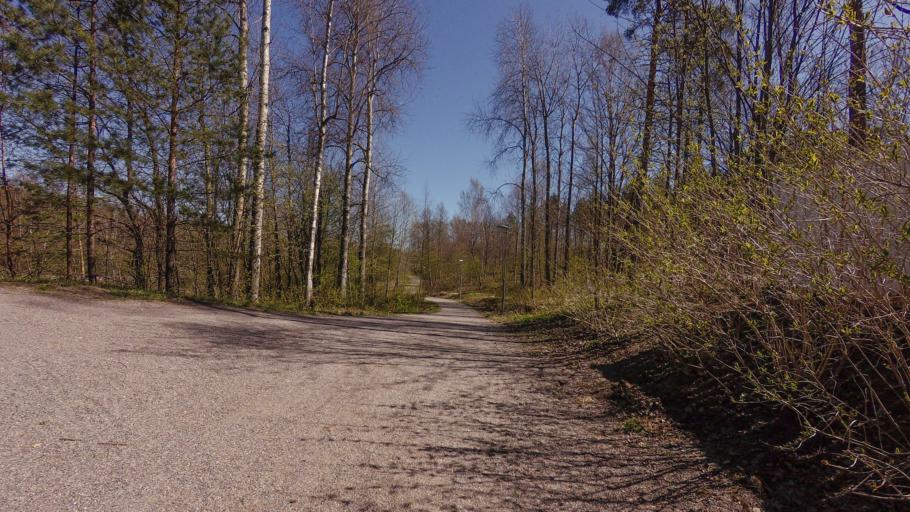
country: FI
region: Uusimaa
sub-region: Helsinki
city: Vantaa
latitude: 60.2314
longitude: 25.1145
